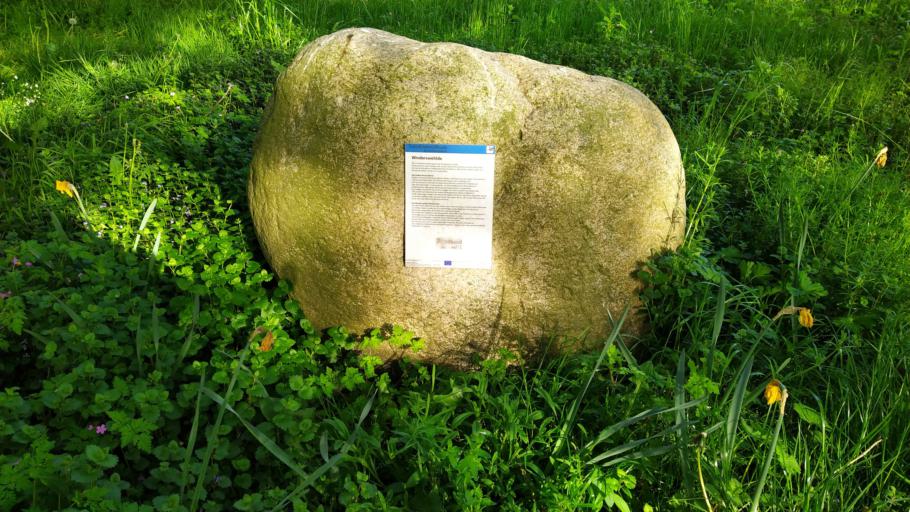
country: DE
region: Lower Saxony
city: Brest
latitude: 53.3998
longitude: 9.3614
